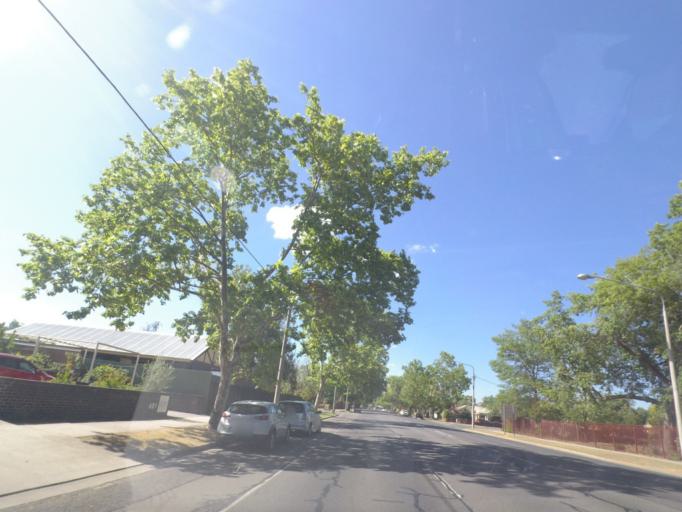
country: AU
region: New South Wales
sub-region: Albury Municipality
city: Albury
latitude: -36.0724
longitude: 146.9258
